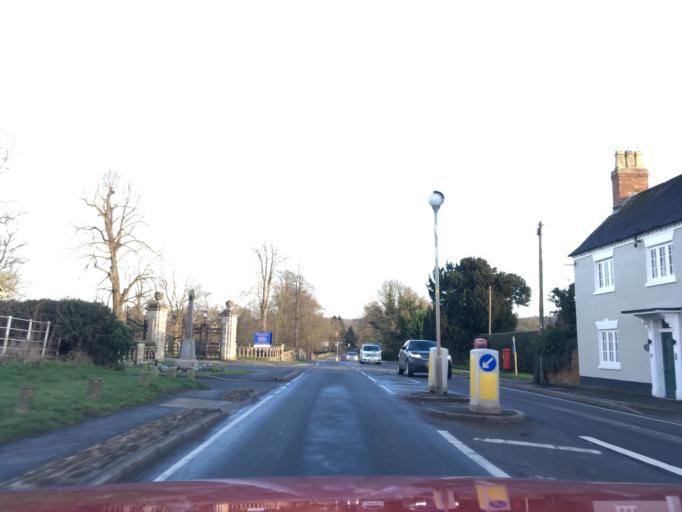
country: GB
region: England
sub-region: Warwickshire
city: Henley in Arden
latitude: 52.2667
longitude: -1.7773
